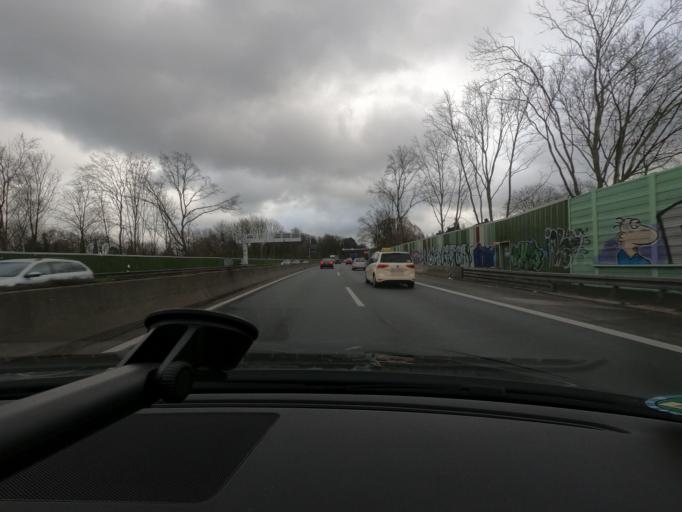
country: DE
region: North Rhine-Westphalia
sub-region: Regierungsbezirk Arnsberg
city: Bochum
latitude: 51.4980
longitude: 7.2252
